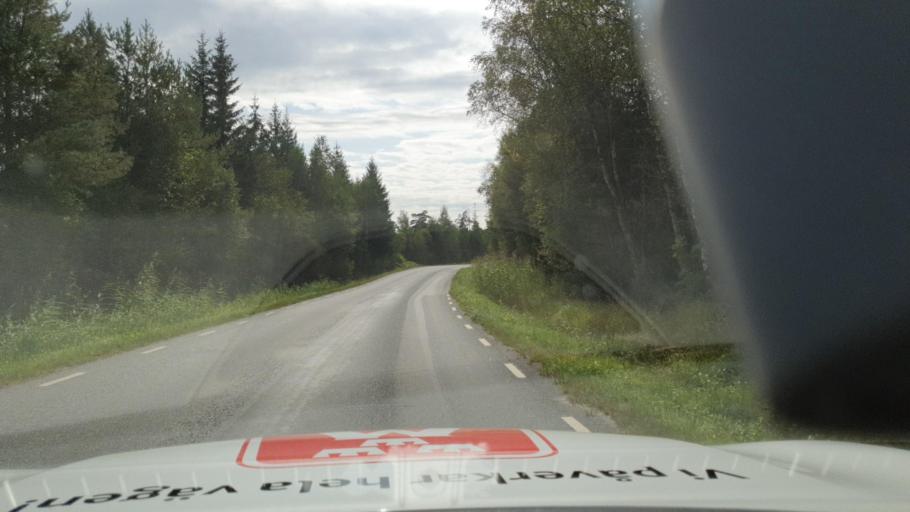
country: SE
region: Vaestra Goetaland
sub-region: Marks Kommun
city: Kinna
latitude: 57.3867
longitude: 12.7706
